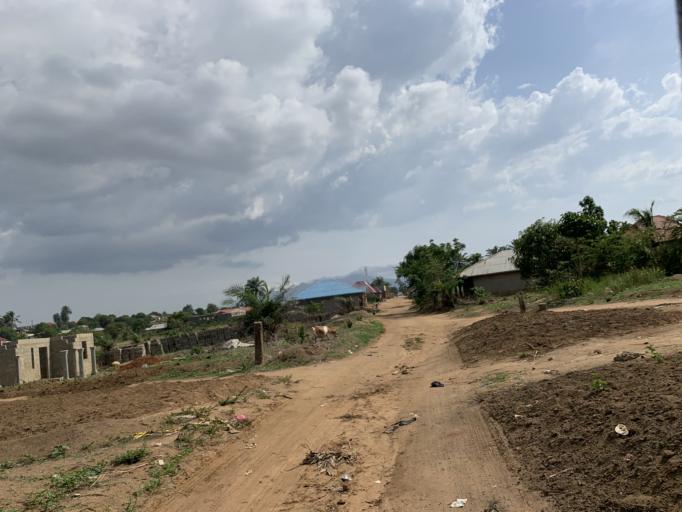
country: SL
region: Western Area
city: Waterloo
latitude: 8.3496
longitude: -13.0361
